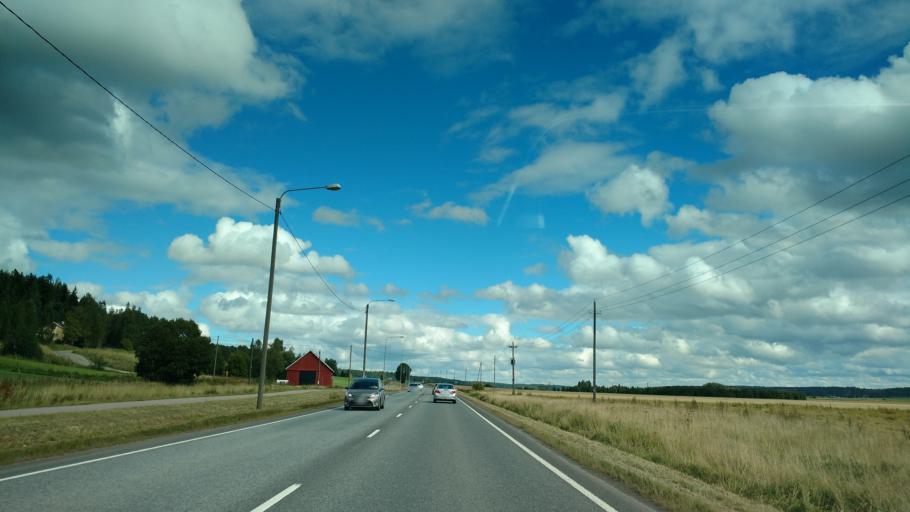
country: FI
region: Varsinais-Suomi
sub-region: Salo
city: Salo
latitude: 60.4058
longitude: 23.1518
